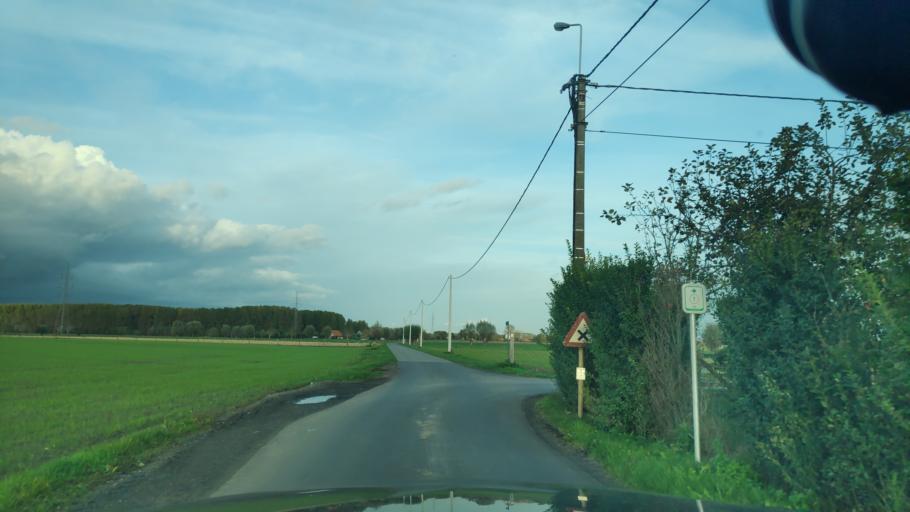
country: BE
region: Flanders
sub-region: Provincie Oost-Vlaanderen
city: Aalter
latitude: 51.1101
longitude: 3.4810
